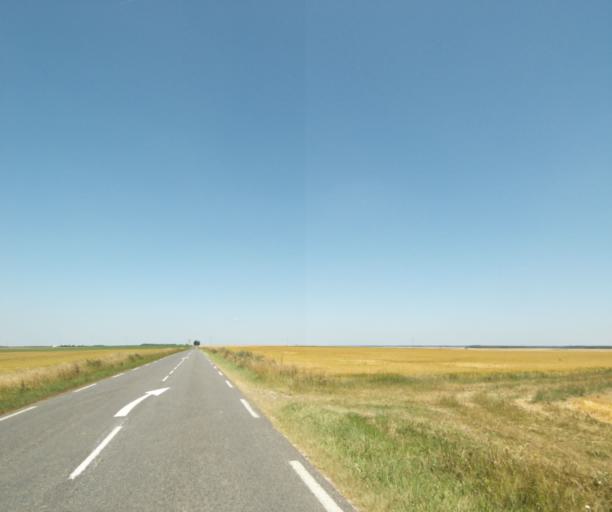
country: FR
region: Centre
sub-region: Departement du Loiret
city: Malesherbes
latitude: 48.3289
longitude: 2.4491
